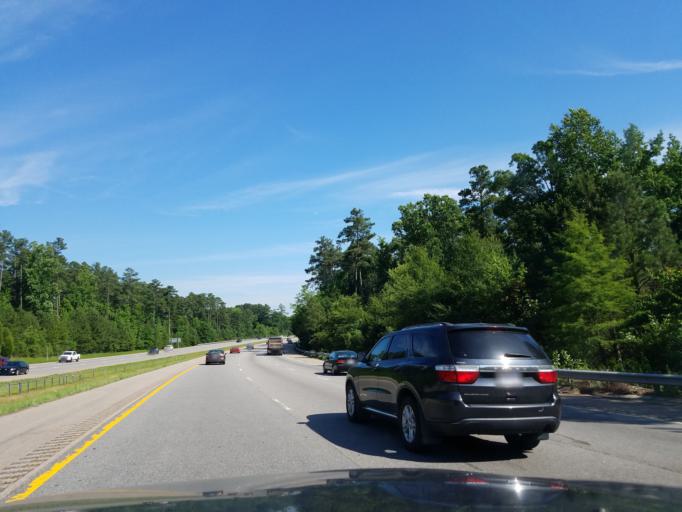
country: US
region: North Carolina
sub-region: Wake County
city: Wake Forest
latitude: 35.8910
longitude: -78.5951
